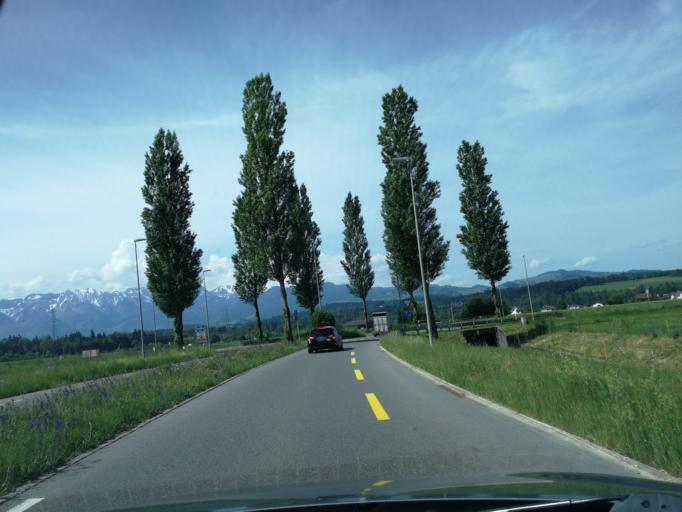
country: CH
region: Bern
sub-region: Thun District
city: Uttigen
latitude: 46.8171
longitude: 7.5902
